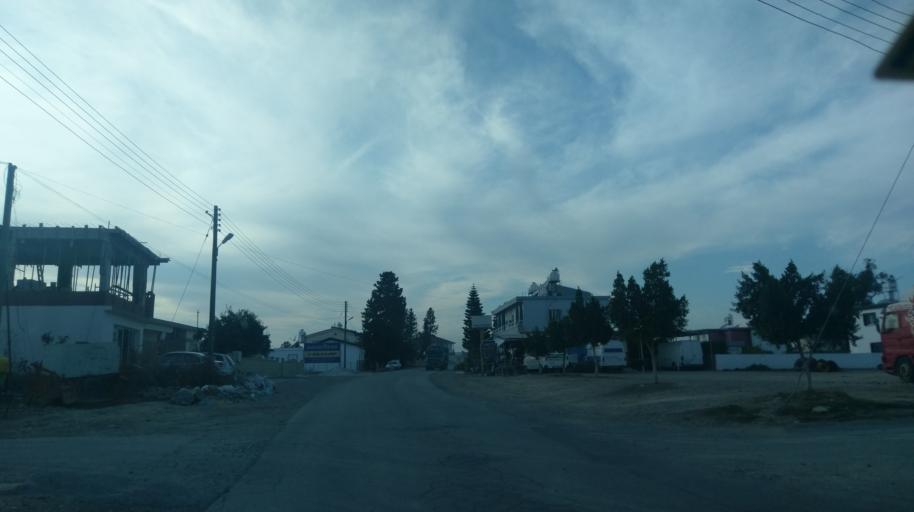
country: CY
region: Larnaka
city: Pergamos
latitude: 35.1295
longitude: 33.6560
